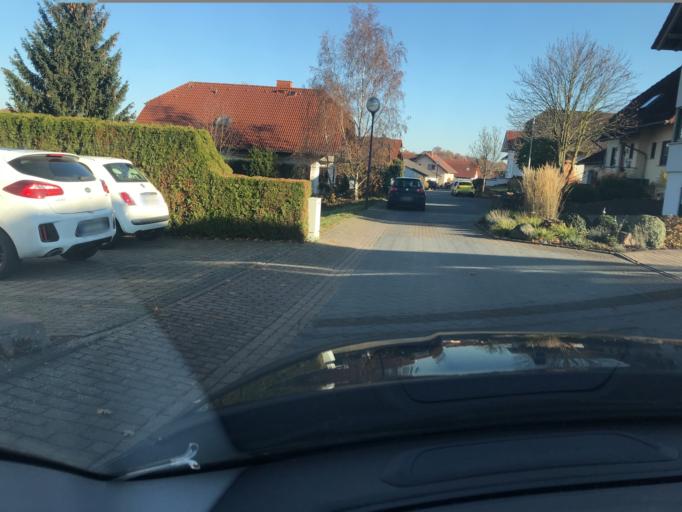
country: DE
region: Rheinland-Pfalz
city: Eppenrod
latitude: 50.4245
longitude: 7.9328
